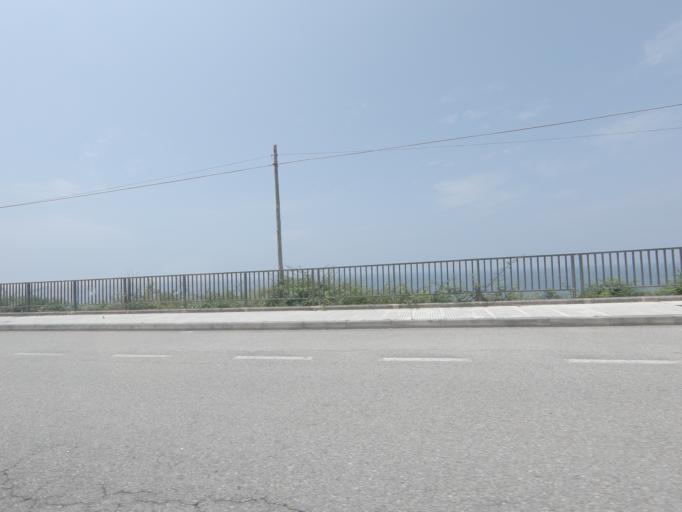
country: ES
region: Galicia
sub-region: Provincia de Pontevedra
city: A Guarda
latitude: 41.8921
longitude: -8.8774
